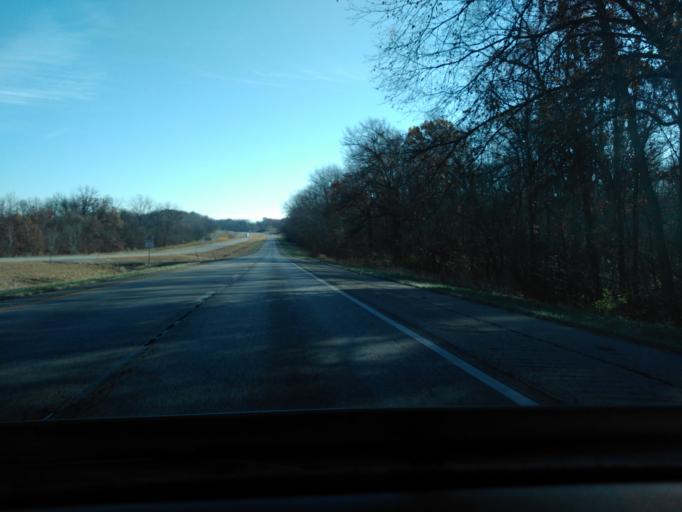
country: US
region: Illinois
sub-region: Bond County
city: Greenville
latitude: 38.8341
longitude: -89.5281
